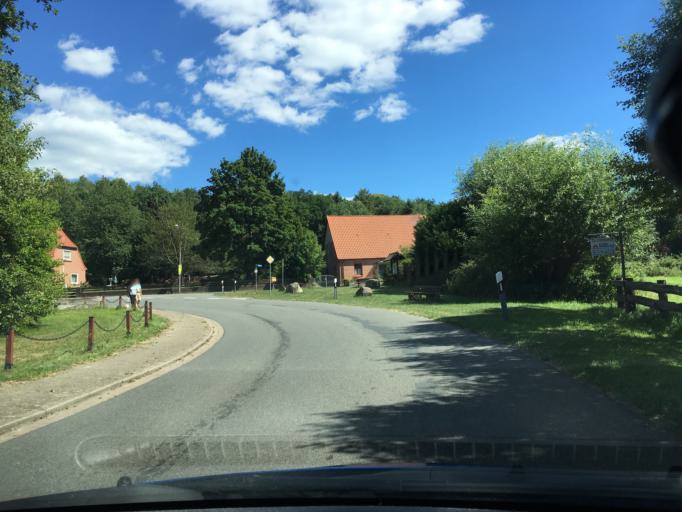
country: DE
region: Lower Saxony
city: Tosterglope
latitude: 53.2012
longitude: 10.8550
